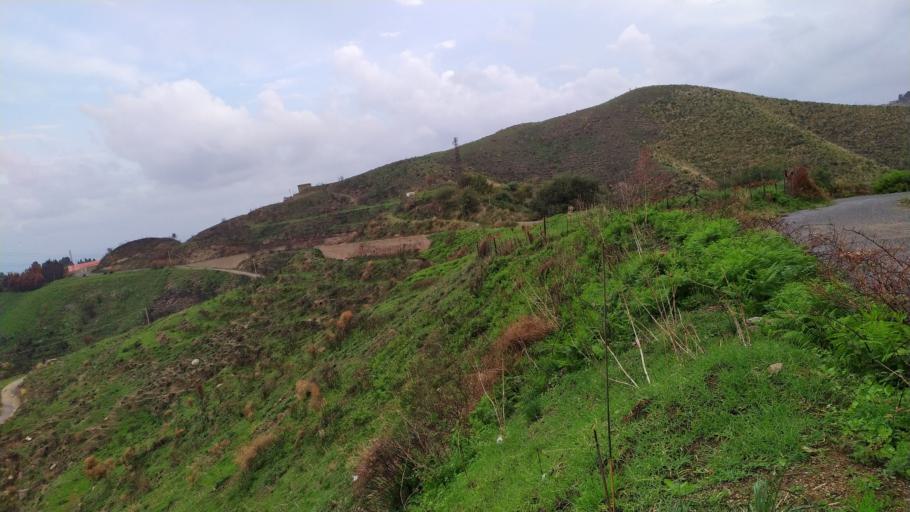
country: IT
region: Sicily
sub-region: Messina
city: Villafranca Tirrena
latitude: 38.2194
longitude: 15.4690
